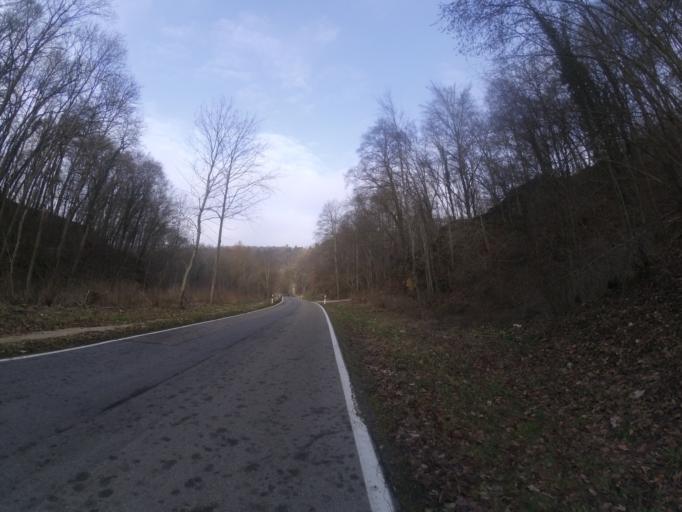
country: DE
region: Baden-Wuerttemberg
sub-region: Tuebingen Region
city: Lauterach
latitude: 48.2581
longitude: 9.5759
